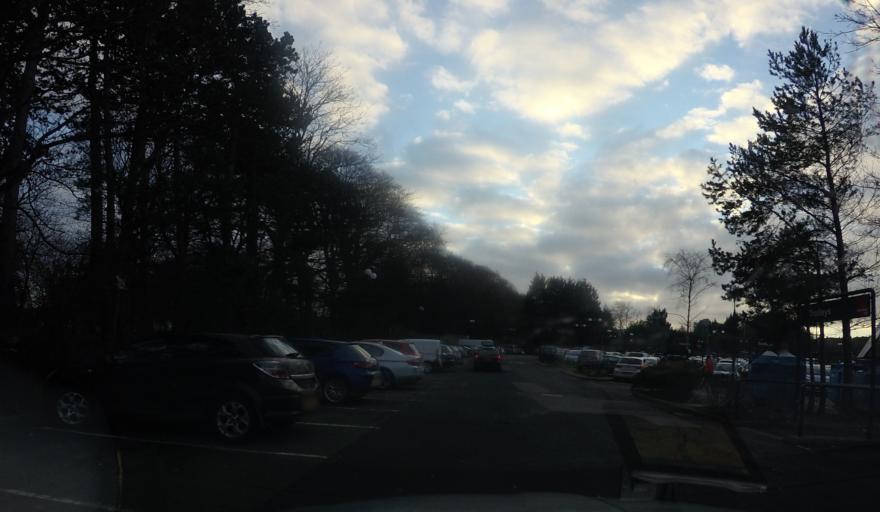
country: GB
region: Scotland
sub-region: West Lothian
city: Seafield
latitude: 55.9260
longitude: -3.1627
